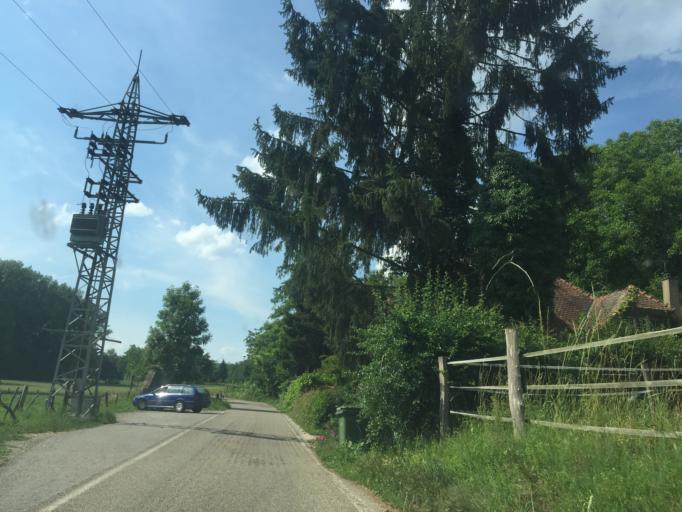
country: DE
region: Baden-Wuerttemberg
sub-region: Karlsruhe Region
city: Dielheim
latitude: 49.3169
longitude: 8.7434
